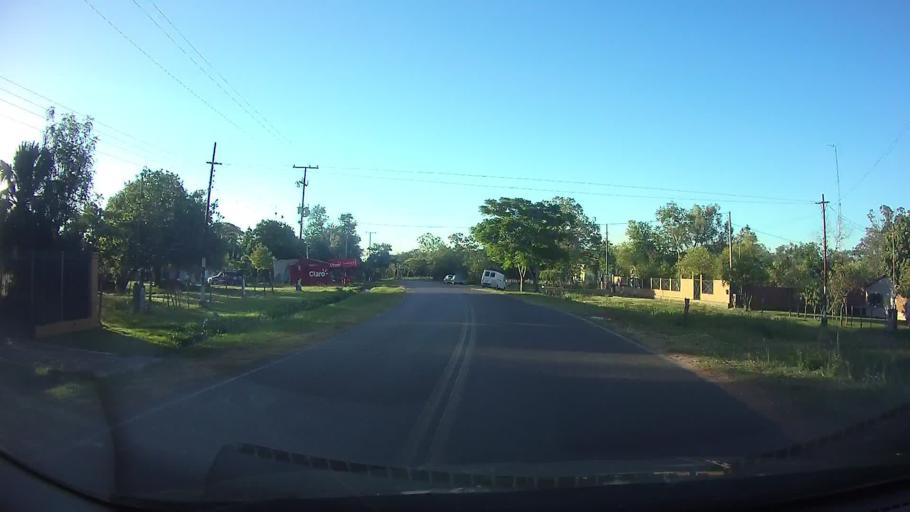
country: PY
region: Central
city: Aregua
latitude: -25.2655
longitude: -57.4136
